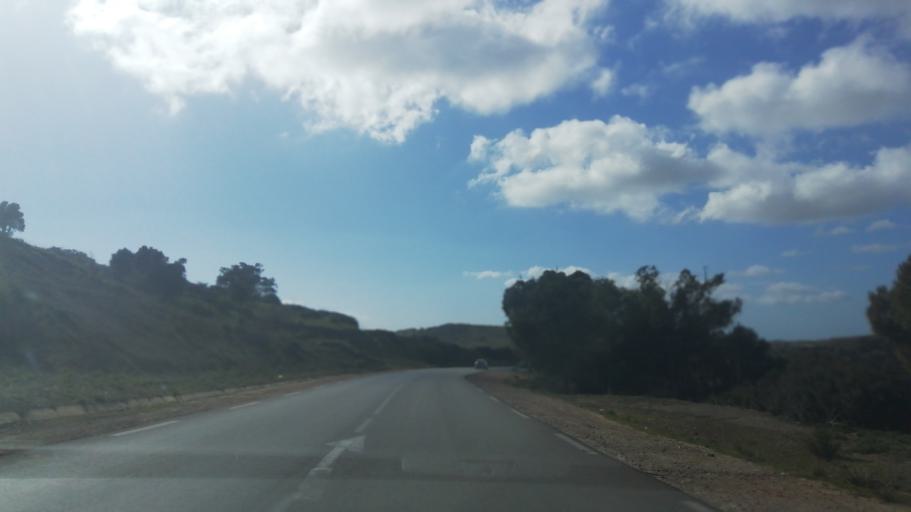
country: DZ
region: Relizane
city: Relizane
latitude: 36.0902
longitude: 0.4711
